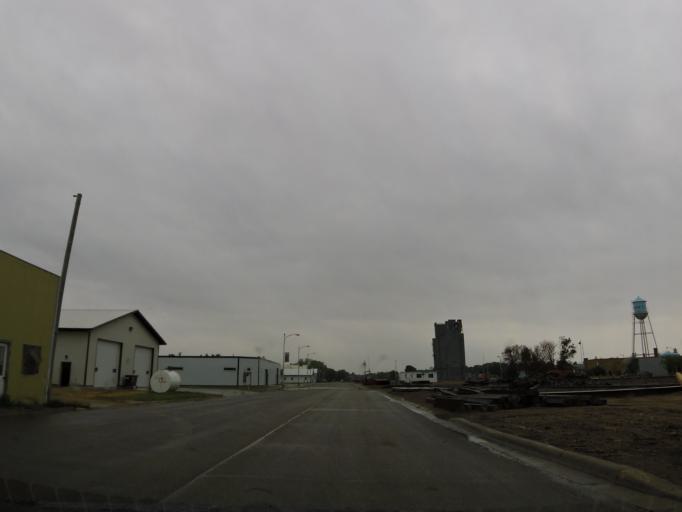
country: US
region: Minnesota
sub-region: Marshall County
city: Warren
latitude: 48.4521
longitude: -96.8736
